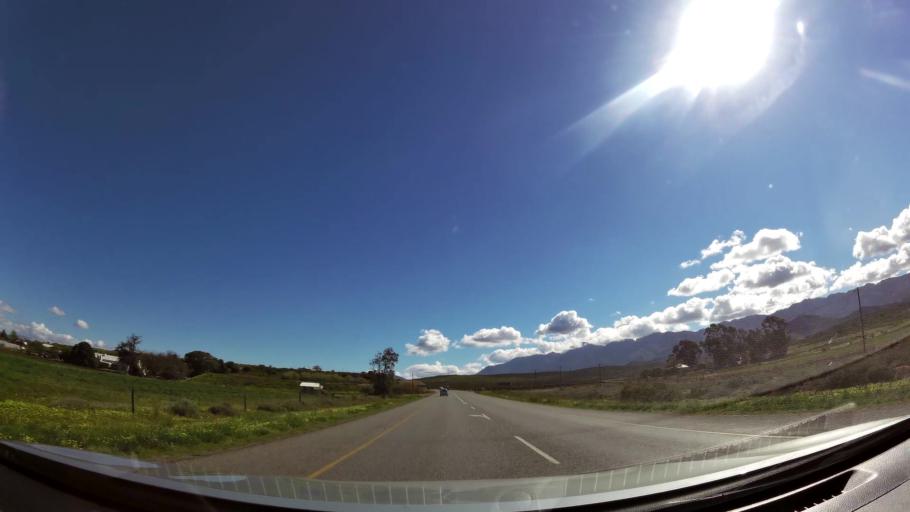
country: ZA
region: Western Cape
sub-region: Cape Winelands District Municipality
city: Ashton
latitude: -33.8215
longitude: 19.9745
